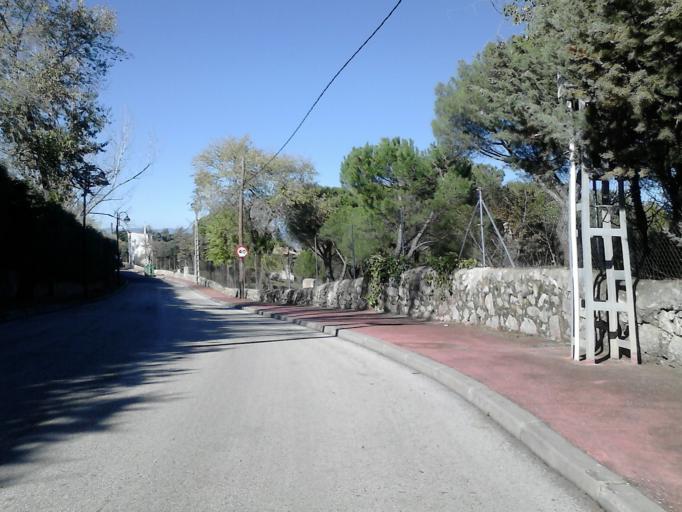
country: ES
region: Madrid
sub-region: Provincia de Madrid
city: Galapagar
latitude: 40.5694
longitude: -3.9920
